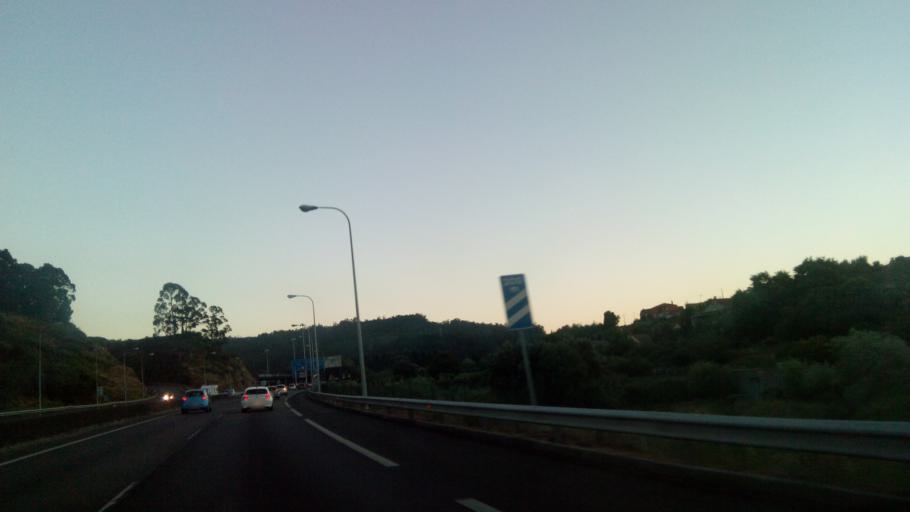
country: ES
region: Galicia
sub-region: Provincia de Pontevedra
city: Pontevedra
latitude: 42.4187
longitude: -8.6511
